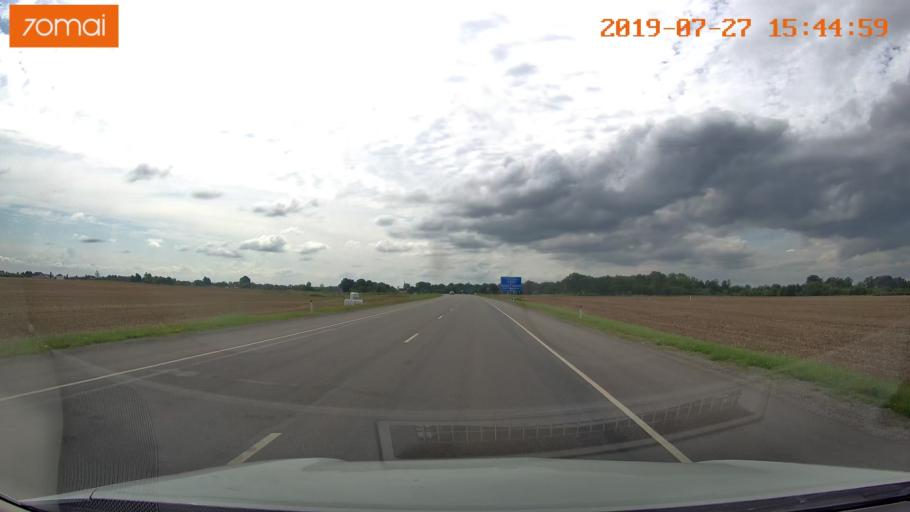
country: RU
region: Kaliningrad
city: Gusev
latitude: 54.6144
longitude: 22.1504
